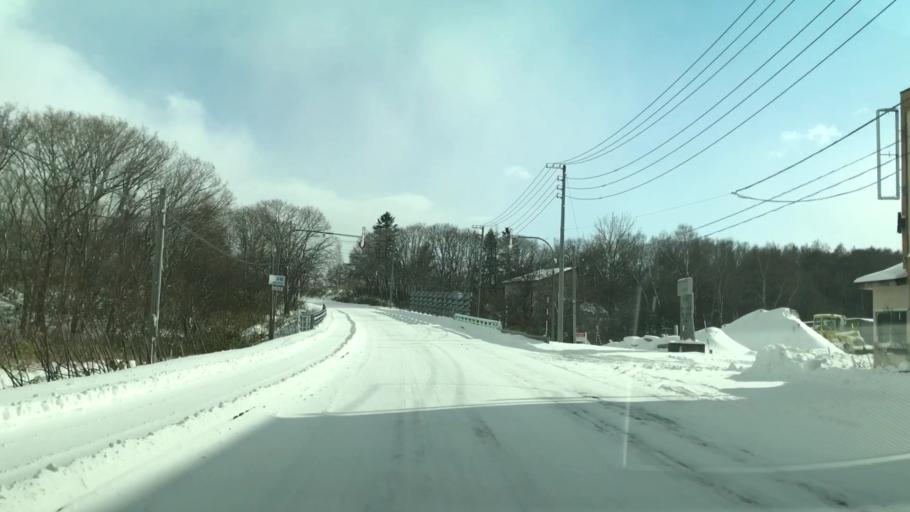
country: JP
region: Hokkaido
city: Yoichi
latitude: 43.3058
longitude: 140.5569
